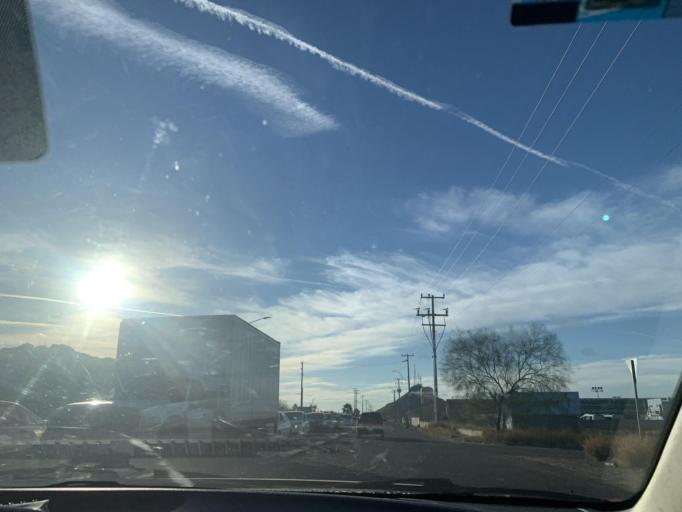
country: MX
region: Sonora
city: Hermosillo
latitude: 29.0741
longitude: -110.9240
